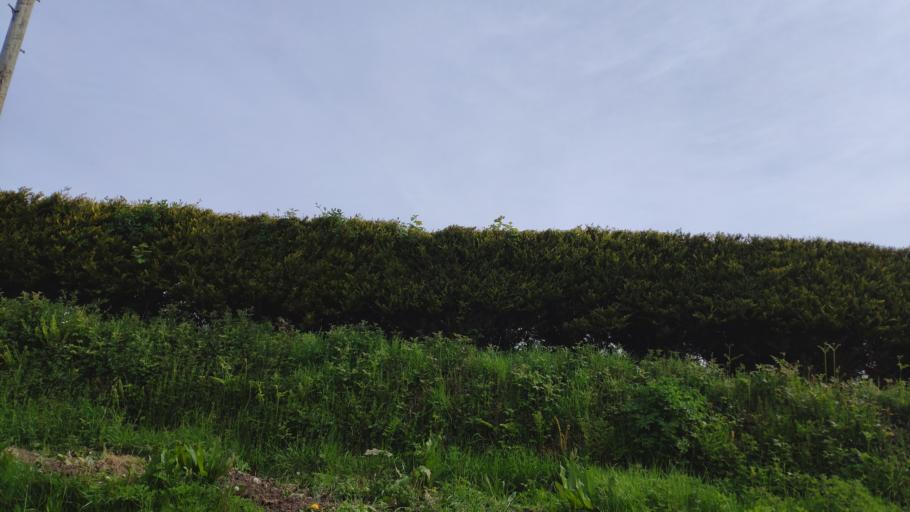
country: IE
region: Munster
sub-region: County Cork
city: Blarney
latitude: 51.9580
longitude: -8.5103
